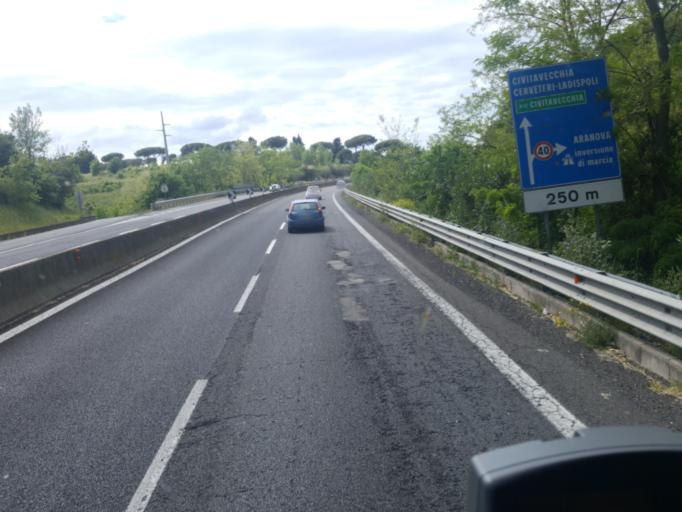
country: IT
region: Latium
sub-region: Citta metropolitana di Roma Capitale
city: Ara Nova
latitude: 41.9107
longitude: 12.2545
